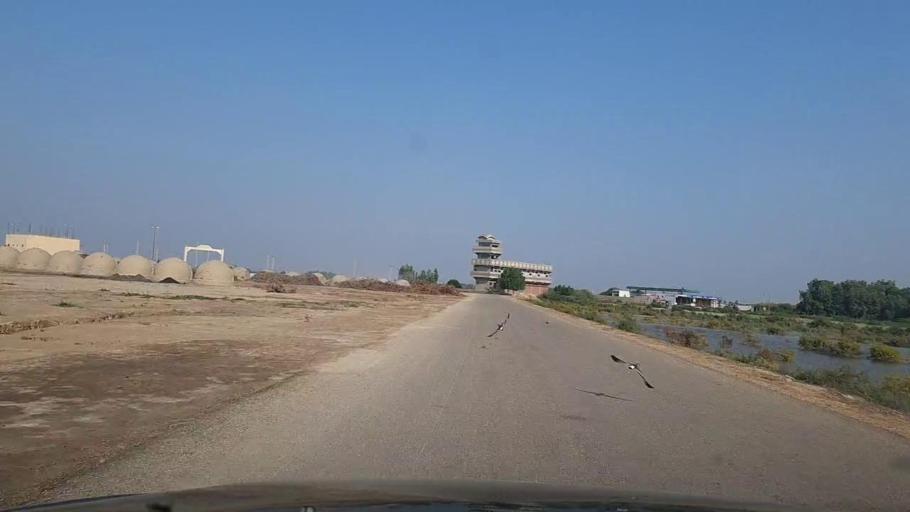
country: PK
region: Sindh
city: Mirpur Batoro
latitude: 24.5912
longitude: 68.0889
